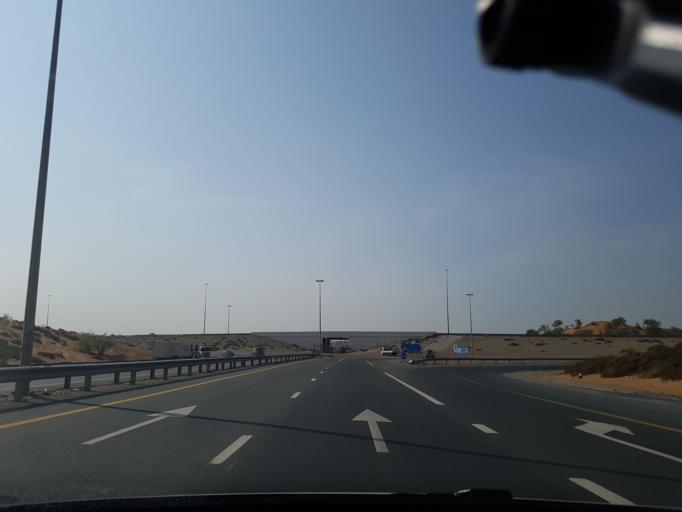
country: AE
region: Umm al Qaywayn
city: Umm al Qaywayn
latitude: 25.5276
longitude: 55.7260
